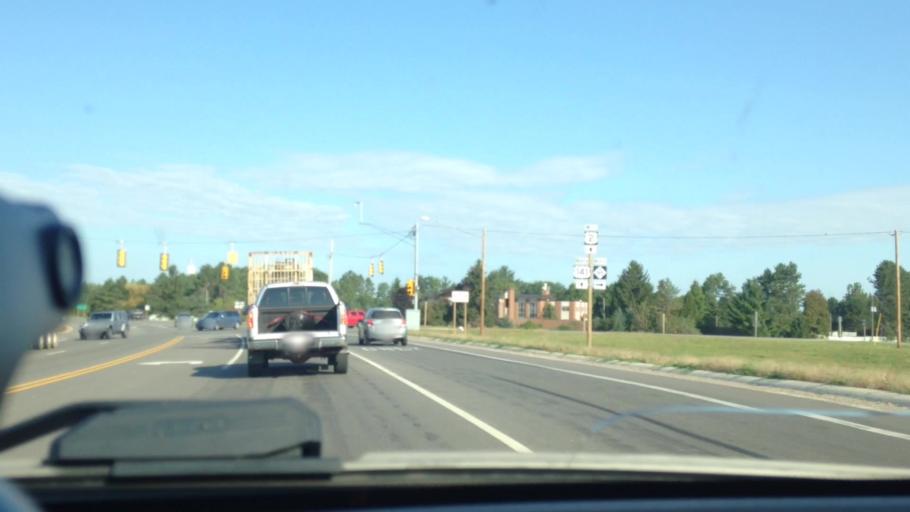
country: US
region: Michigan
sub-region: Dickinson County
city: Iron Mountain
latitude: 45.8627
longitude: -88.0610
